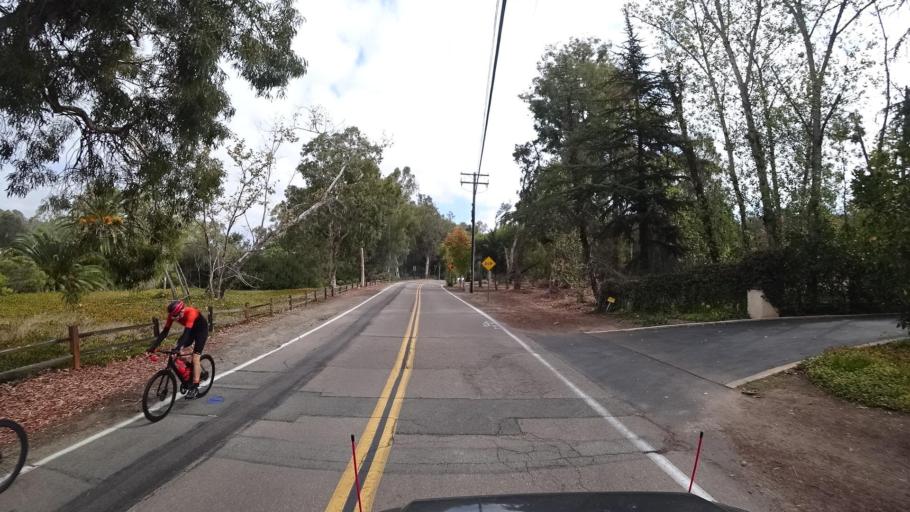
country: US
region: California
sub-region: San Diego County
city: Rancho Santa Fe
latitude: 33.0145
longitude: -117.2318
